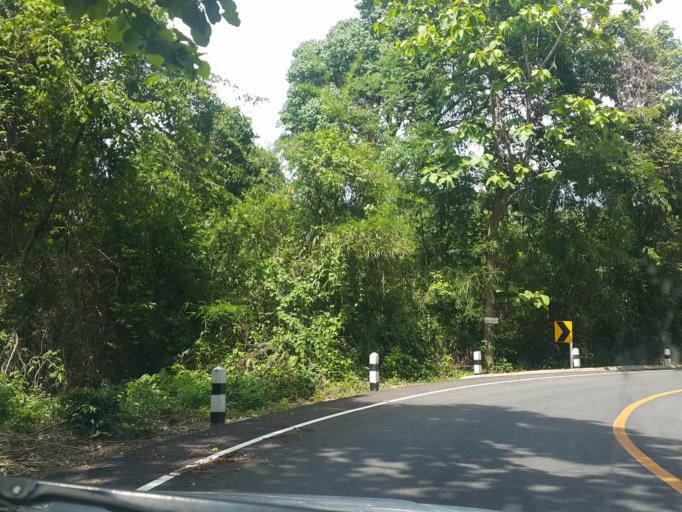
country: TH
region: Nan
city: Ban Luang
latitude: 18.8731
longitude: 100.5181
